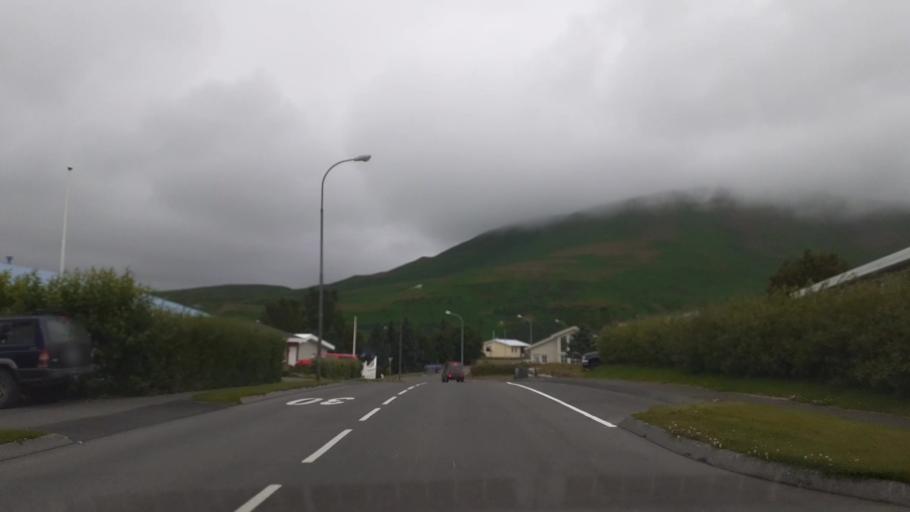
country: IS
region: Northeast
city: Husavik
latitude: 66.0383
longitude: -17.3360
